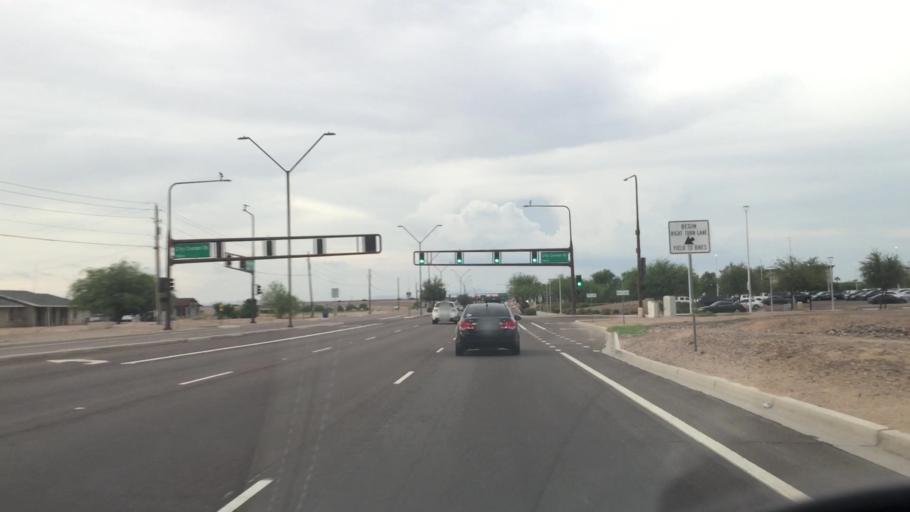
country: US
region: Arizona
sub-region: Maricopa County
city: Avondale
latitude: 33.4525
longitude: -112.3063
